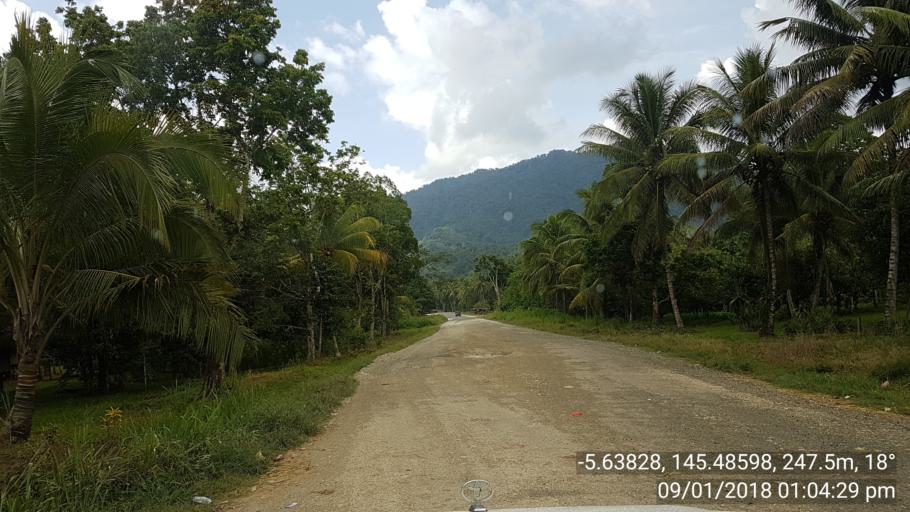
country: PG
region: Eastern Highlands
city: Goroka
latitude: -5.6384
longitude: 145.4861
